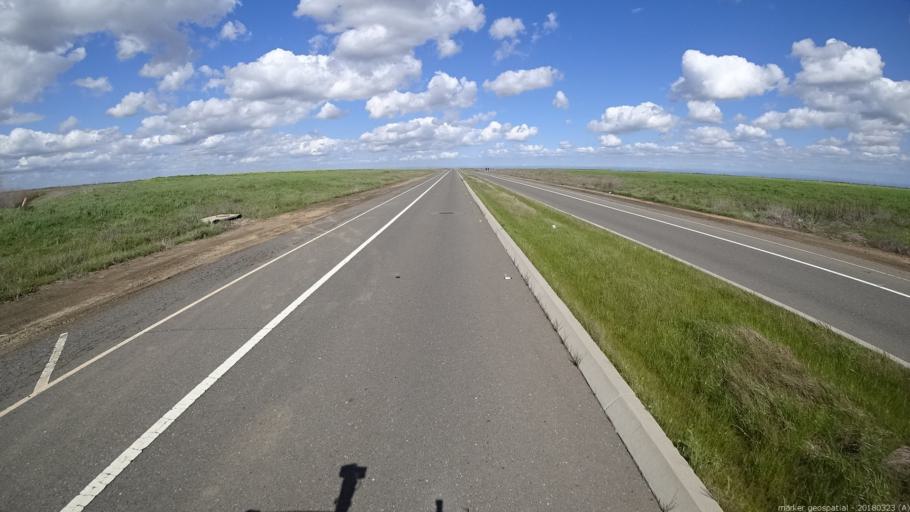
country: US
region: California
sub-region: Sacramento County
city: Elverta
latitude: 38.7003
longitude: -121.5690
